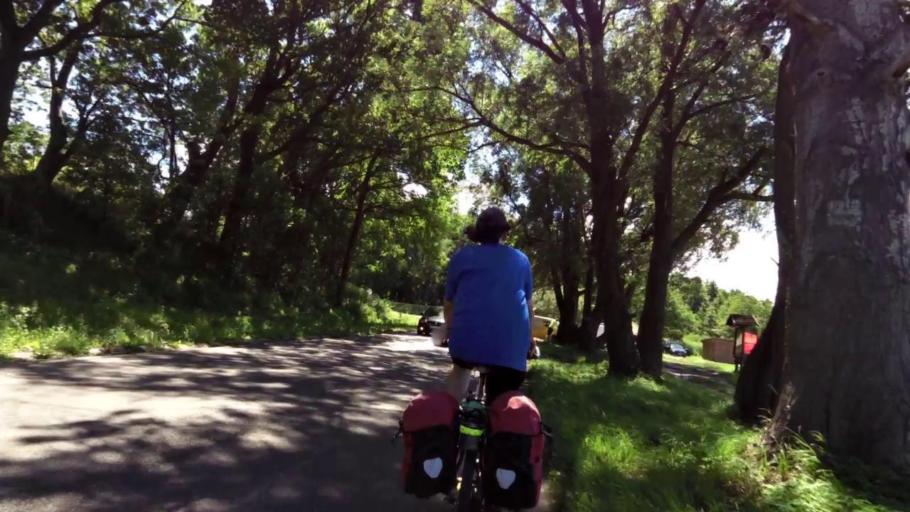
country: PL
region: West Pomeranian Voivodeship
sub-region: Koszalin
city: Koszalin
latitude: 54.2841
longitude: 16.2096
